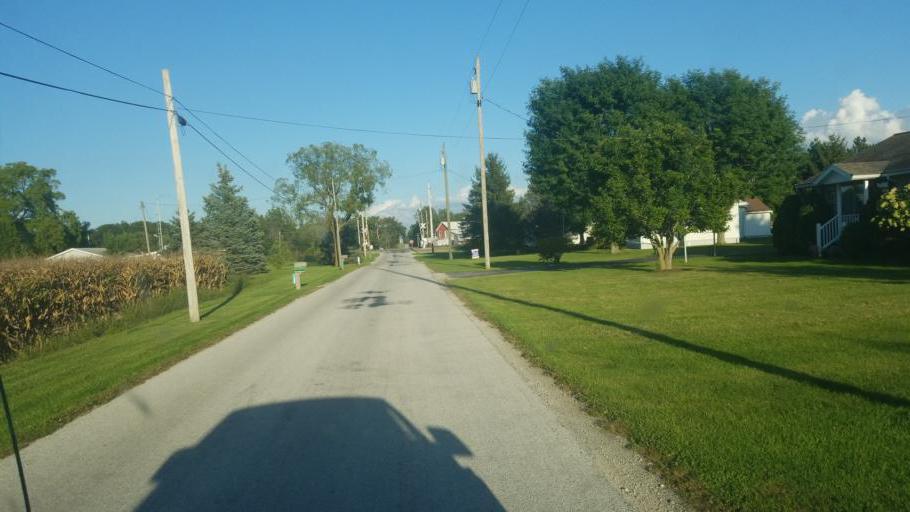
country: US
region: Ohio
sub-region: Wyandot County
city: Carey
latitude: 40.8907
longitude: -83.3332
